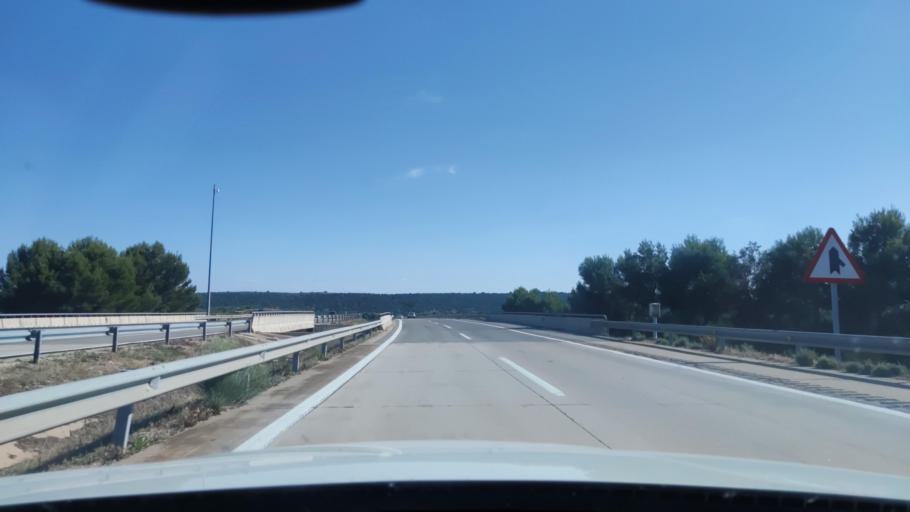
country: ES
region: Castille-La Mancha
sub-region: Provincia de Cuenca
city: Sisante
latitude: 39.4096
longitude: -2.2156
